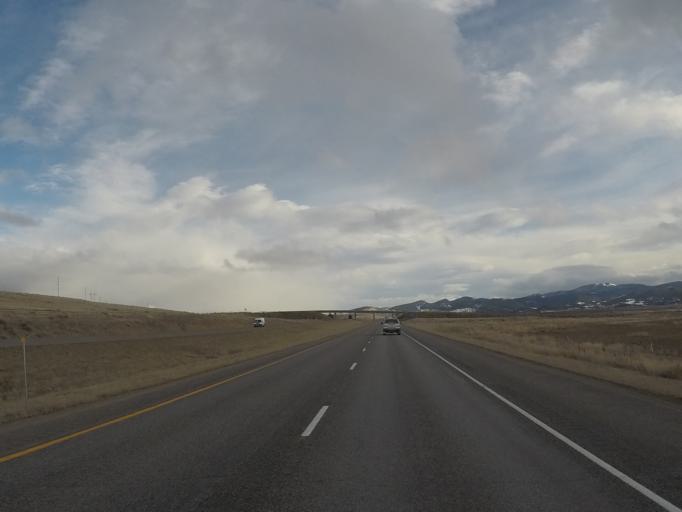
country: US
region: Montana
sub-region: Deer Lodge County
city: Warm Springs
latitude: 46.1117
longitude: -112.7985
